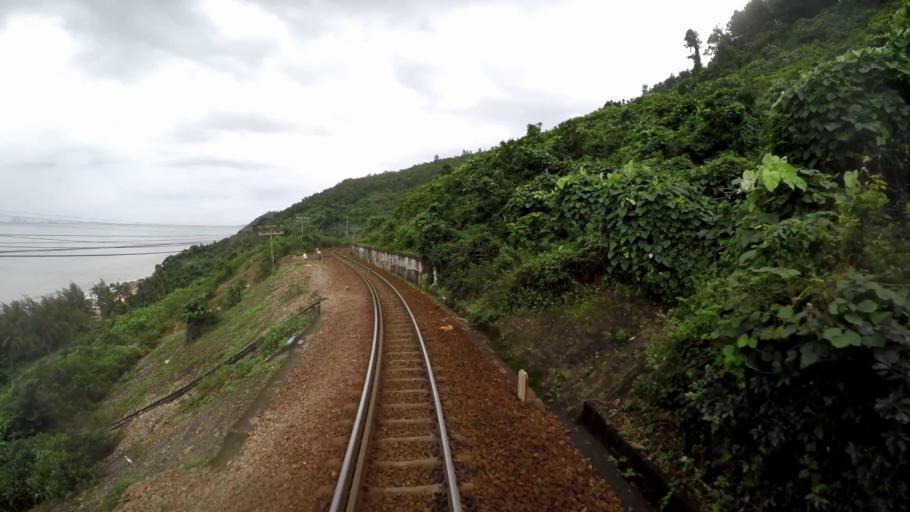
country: VN
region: Da Nang
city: Lien Chieu
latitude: 16.1577
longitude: 108.1351
